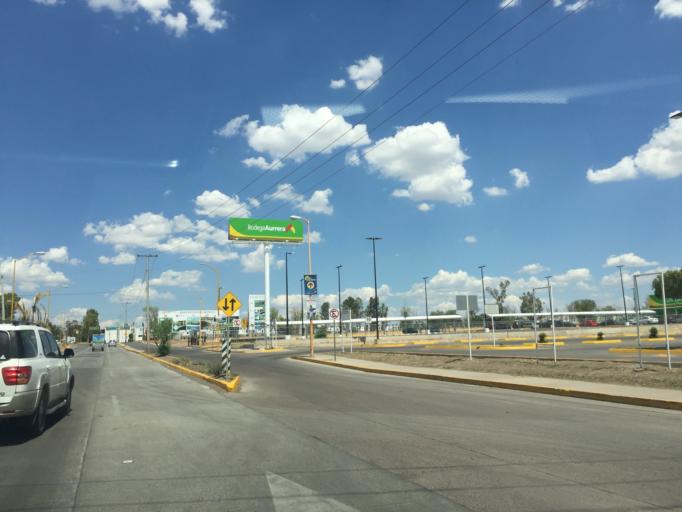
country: MX
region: Aguascalientes
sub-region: Aguascalientes
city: La Loma de los Negritos
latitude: 21.8432
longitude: -102.3229
